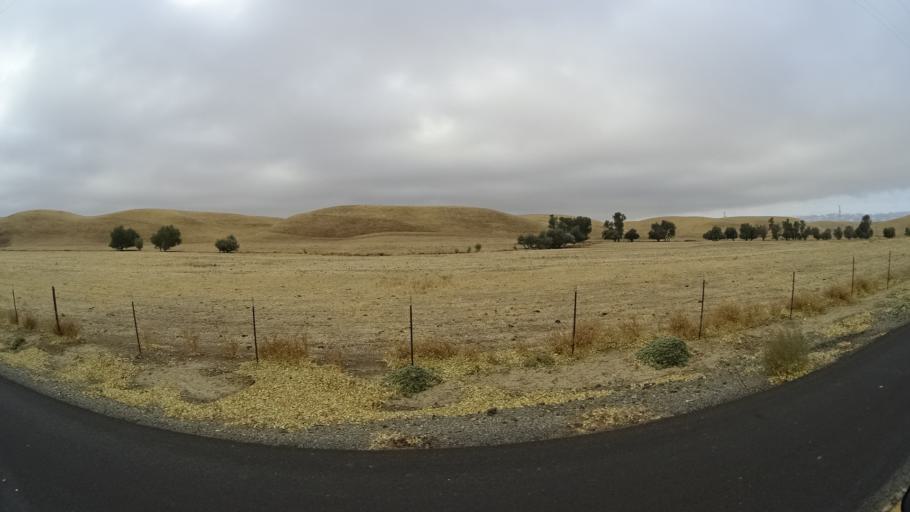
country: US
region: California
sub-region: Yolo County
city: Dunnigan
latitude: 38.8622
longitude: -122.0399
